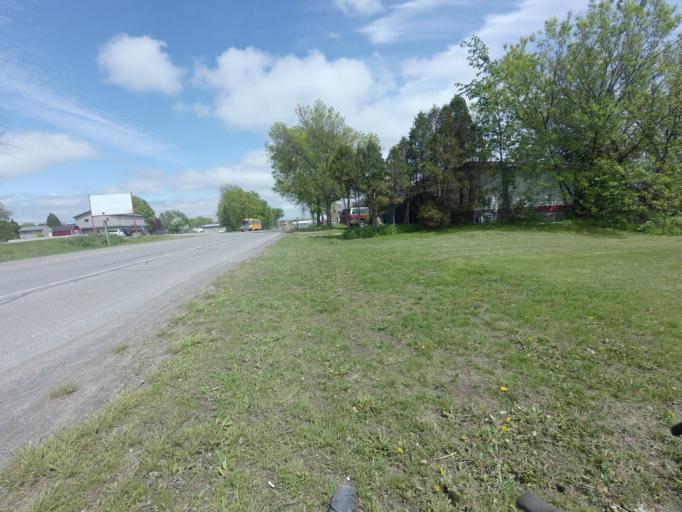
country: CA
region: Ontario
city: Cornwall
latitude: 44.9785
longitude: -74.6874
